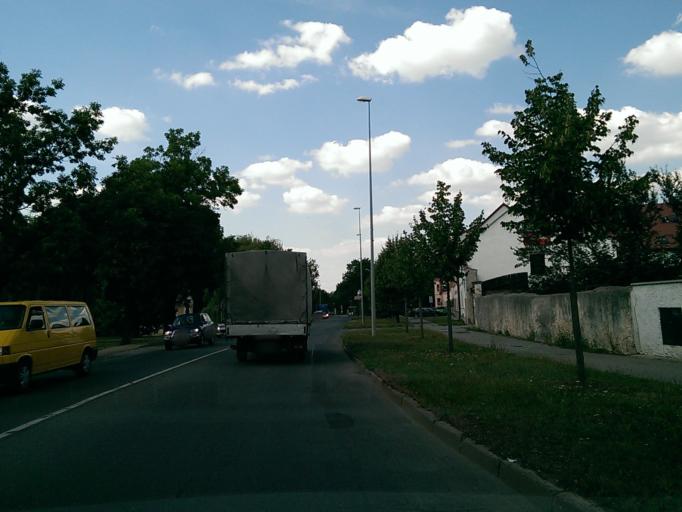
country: CZ
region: Praha
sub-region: Praha 14
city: Dolni Pocernice
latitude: 50.0555
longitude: 14.5630
